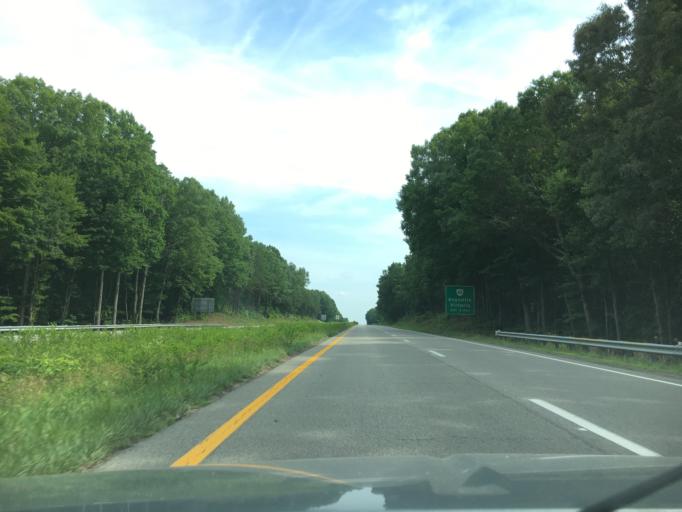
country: US
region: Virginia
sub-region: Charlotte County
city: Charlotte Court House
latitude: 37.0554
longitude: -78.4707
